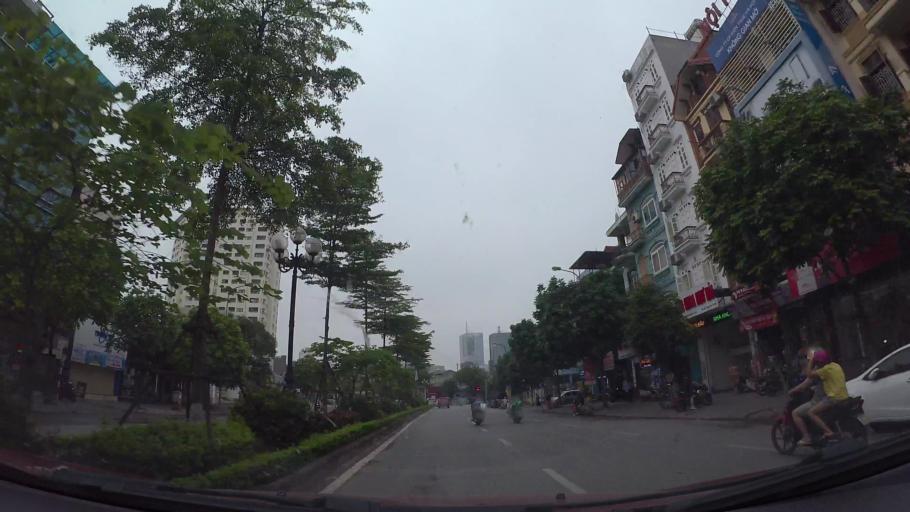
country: VN
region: Ha Noi
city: Cau Giay
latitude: 21.0150
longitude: 105.7950
